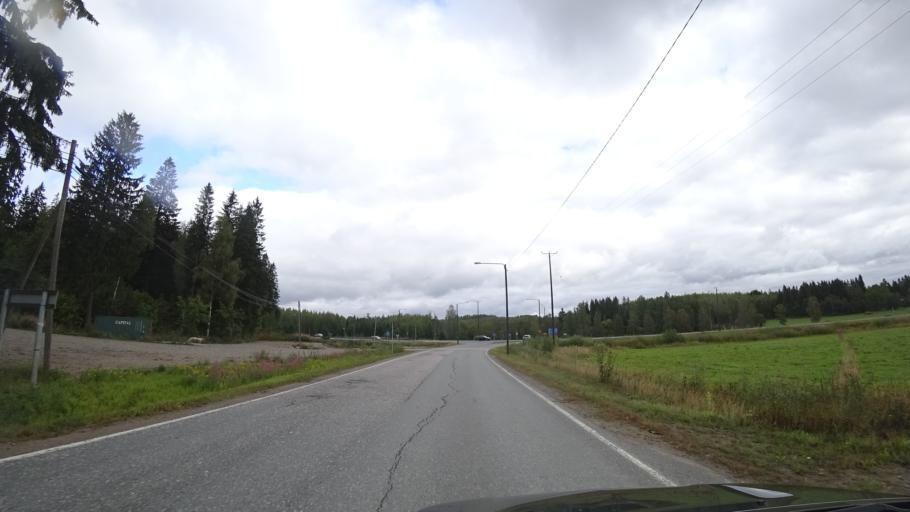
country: FI
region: Haeme
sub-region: Haemeenlinna
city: Lammi
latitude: 61.0507
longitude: 25.0081
